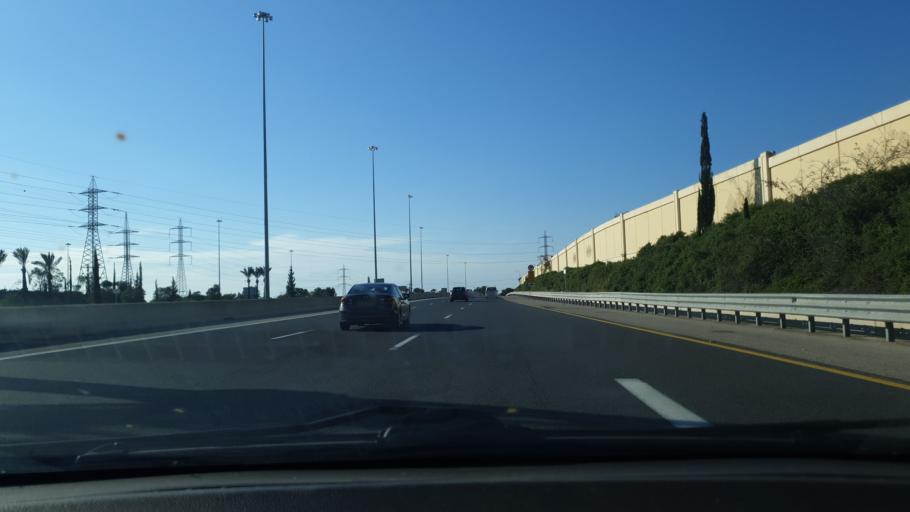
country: IL
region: Central District
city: Rishon LeZiyyon
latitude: 31.9663
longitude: 34.7627
